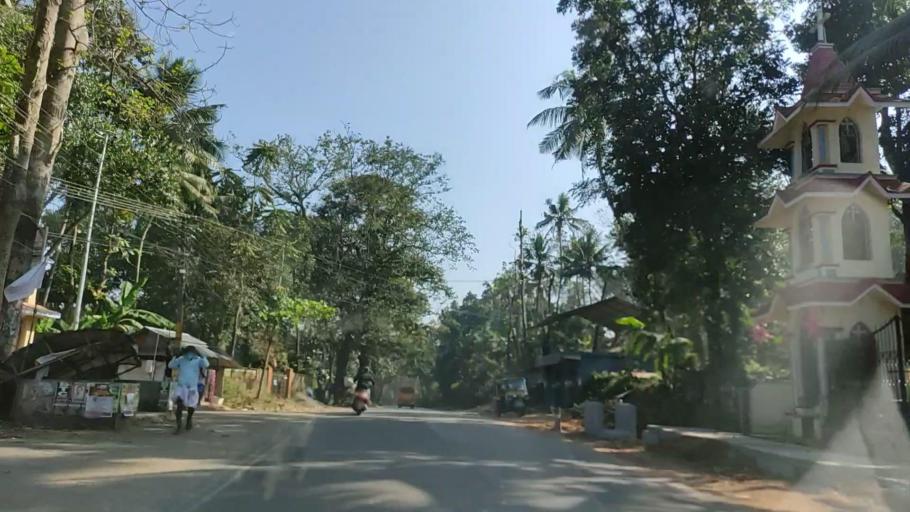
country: IN
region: Kerala
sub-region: Kollam
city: Punalur
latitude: 8.9006
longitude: 76.8648
